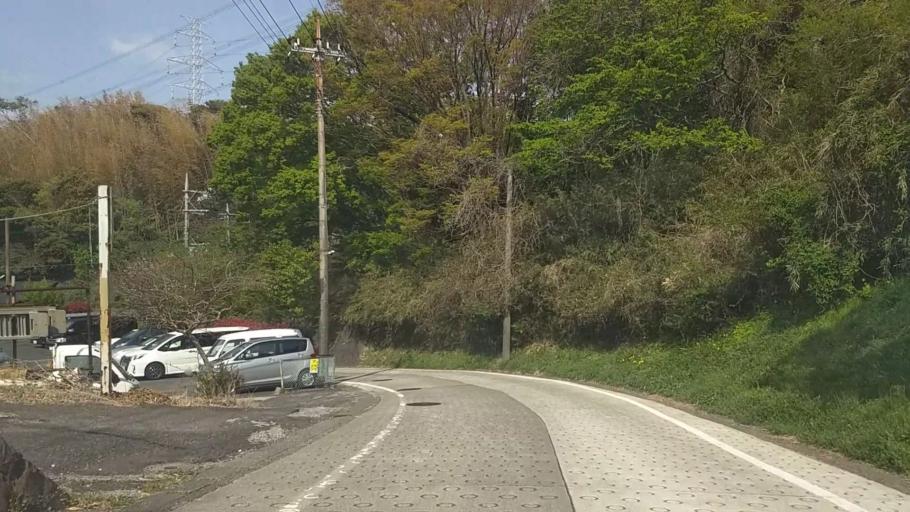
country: JP
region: Kanagawa
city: Kamakura
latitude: 35.3812
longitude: 139.5664
